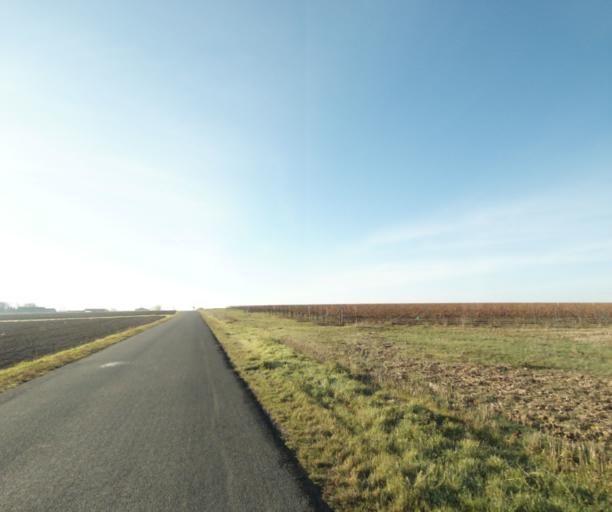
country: FR
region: Poitou-Charentes
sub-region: Departement de la Charente-Maritime
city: Cherac
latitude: 45.6938
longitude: -0.4493
